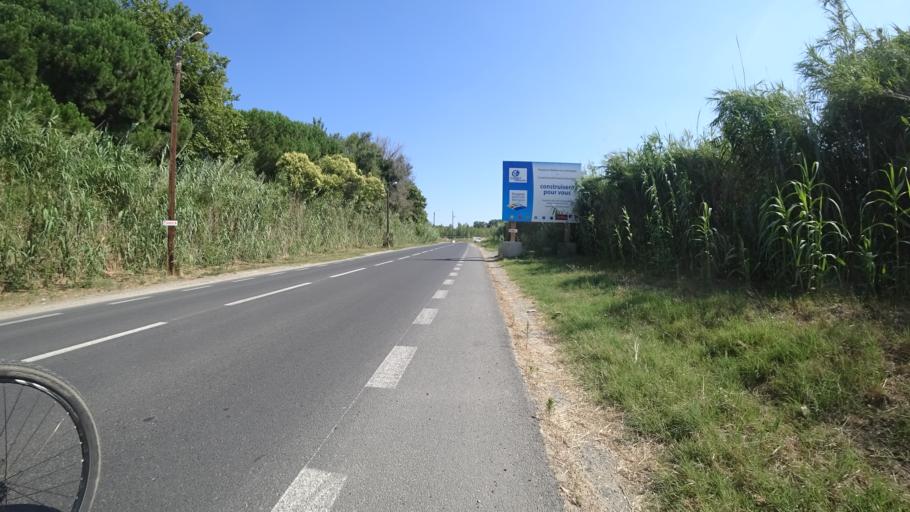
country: FR
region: Languedoc-Roussillon
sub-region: Departement des Pyrenees-Orientales
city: Canet-en-Roussillon
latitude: 42.7058
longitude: 3.0222
